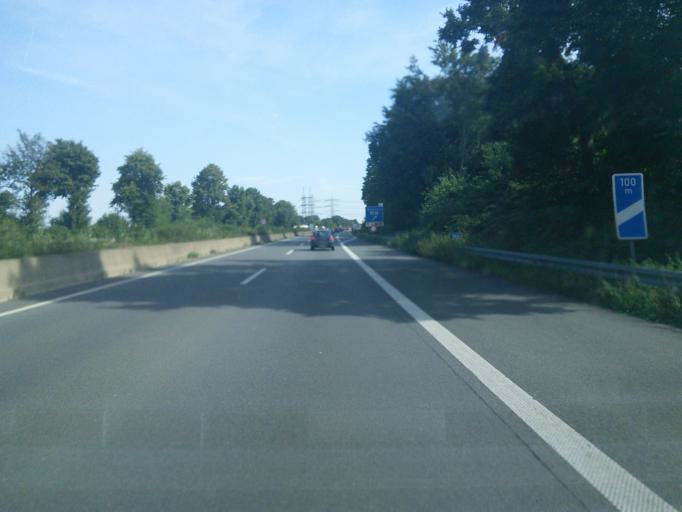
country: DE
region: North Rhine-Westphalia
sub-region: Regierungsbezirk Dusseldorf
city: Dormagen
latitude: 51.1282
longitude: 6.7933
